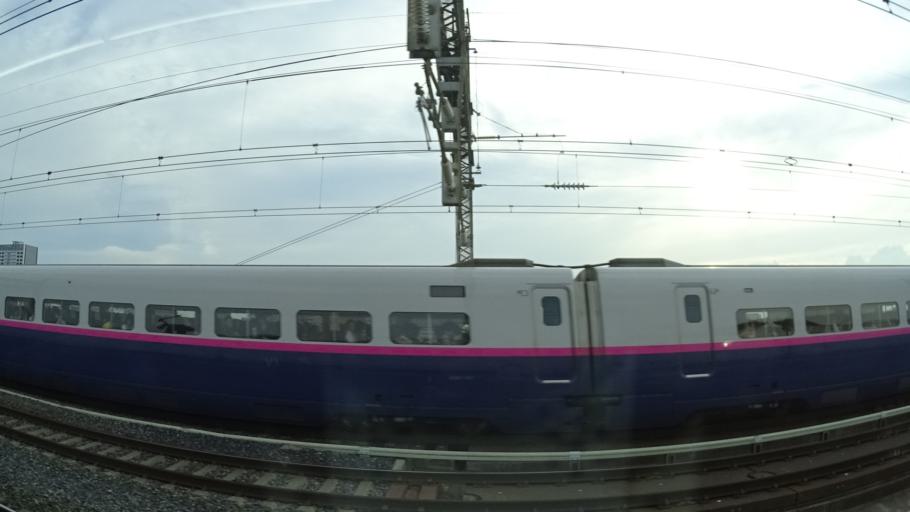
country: JP
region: Saitama
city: Yono
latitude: 35.9114
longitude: 139.6209
